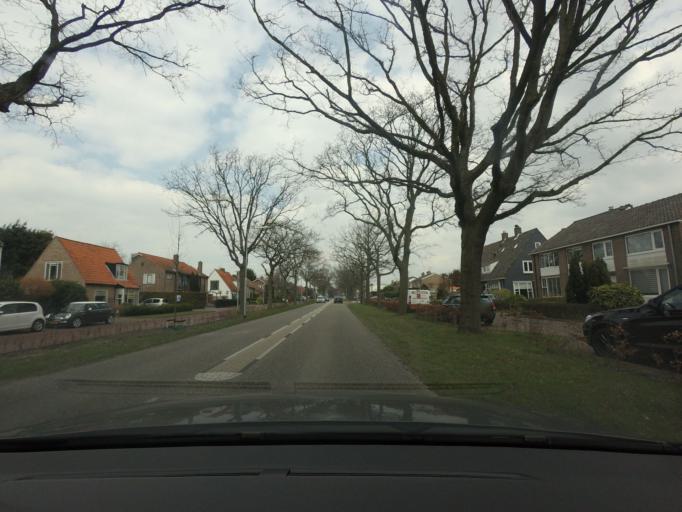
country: NL
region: North Holland
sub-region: Gemeente Alkmaar
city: Alkmaar
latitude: 52.6637
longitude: 4.7131
